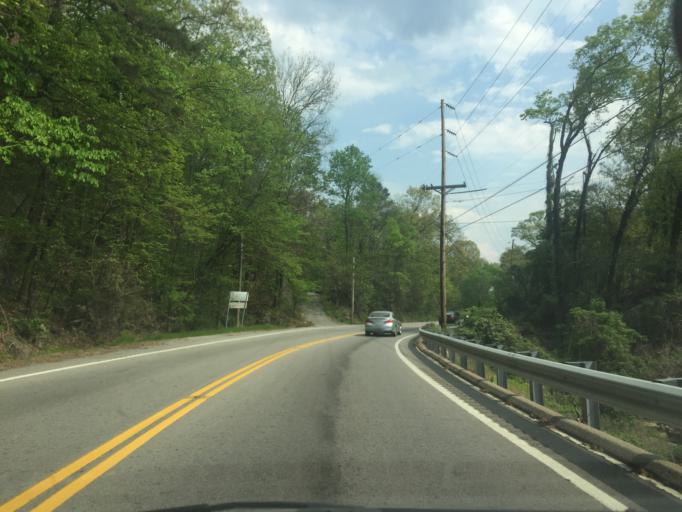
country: US
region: Tennessee
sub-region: Hamilton County
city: Signal Mountain
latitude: 35.1099
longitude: -85.3513
